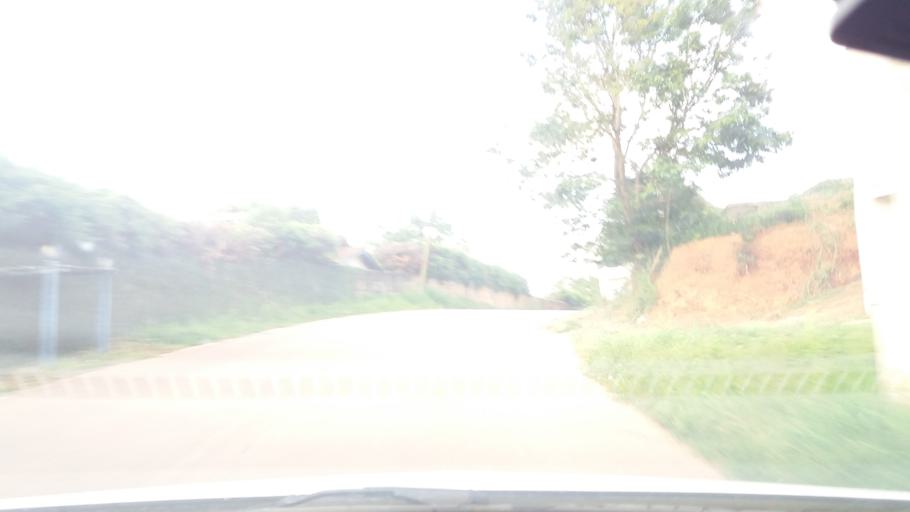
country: BR
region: Sao Paulo
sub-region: Bom Jesus Dos Perdoes
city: Bom Jesus dos Perdoes
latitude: -23.1761
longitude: -46.4836
